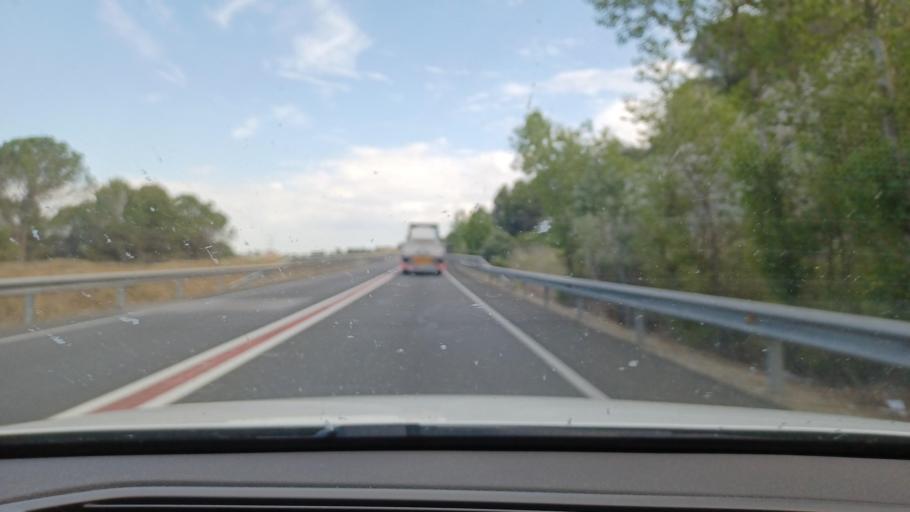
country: ES
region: Catalonia
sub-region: Provincia de Barcelona
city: La Pobla de Claramunt
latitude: 41.5552
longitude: 1.6888
